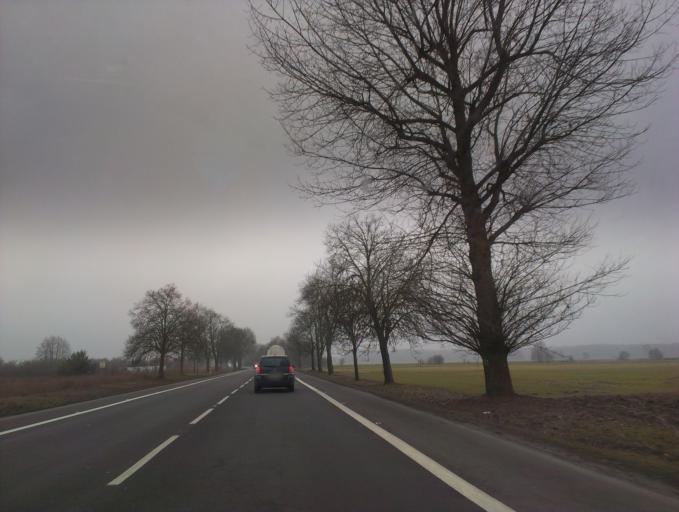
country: PL
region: Greater Poland Voivodeship
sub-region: Powiat pilski
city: Ujscie
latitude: 53.0955
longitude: 16.7420
